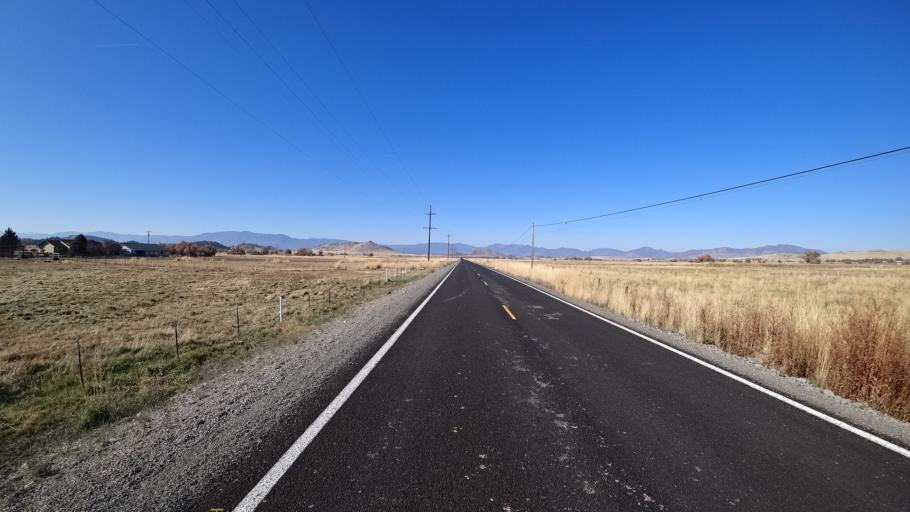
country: US
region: California
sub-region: Siskiyou County
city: Montague
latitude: 41.7114
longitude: -122.4156
